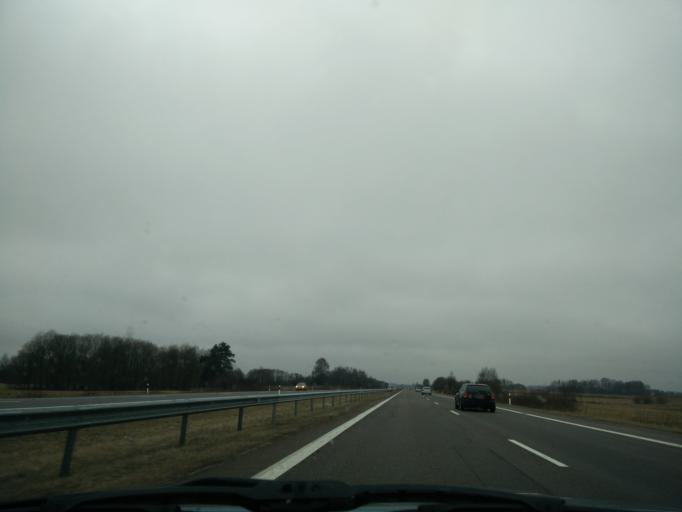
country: LT
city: Skaudvile
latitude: 55.4314
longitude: 22.7487
